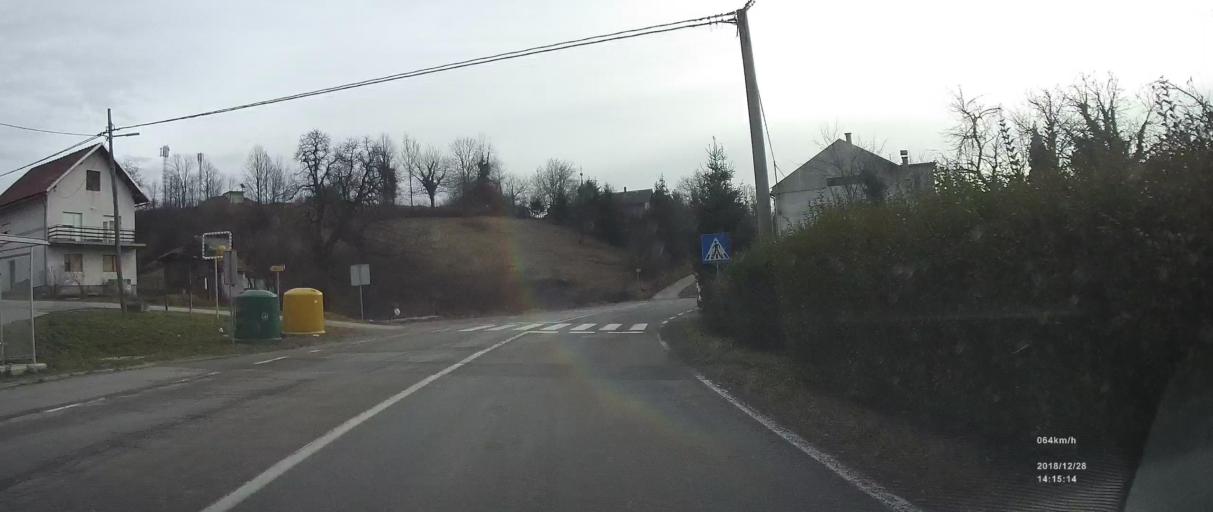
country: HR
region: Primorsko-Goranska
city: Vrbovsko
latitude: 45.4261
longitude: 15.0262
